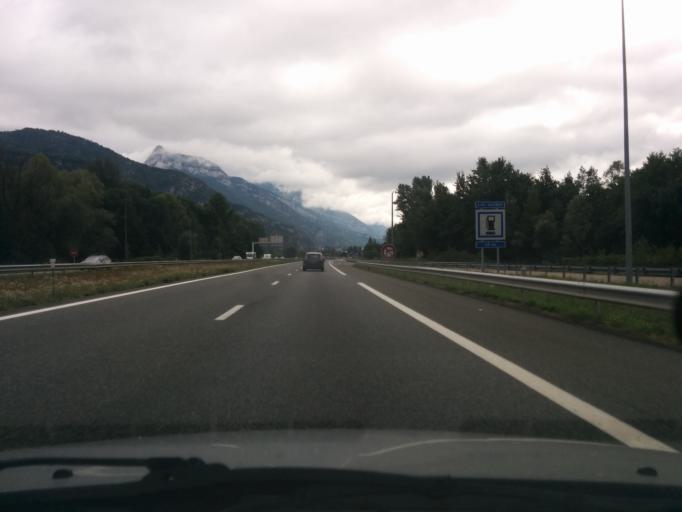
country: FR
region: Rhone-Alpes
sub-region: Departement de l'Isere
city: La Buisse
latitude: 45.3198
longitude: 5.6077
